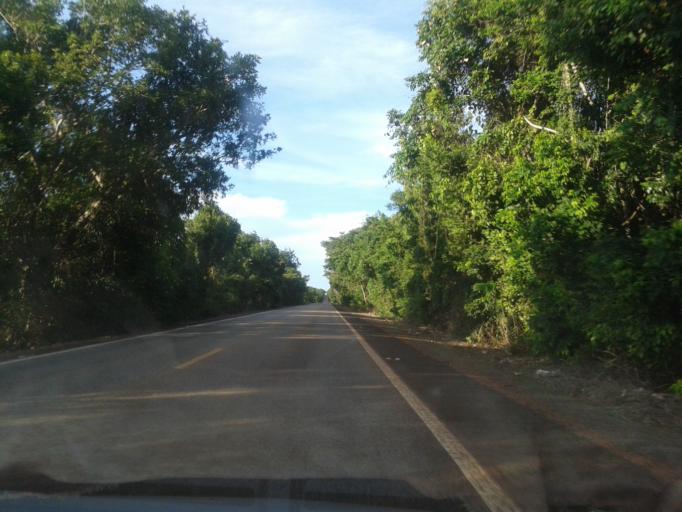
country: BR
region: Goias
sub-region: Sao Miguel Do Araguaia
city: Sao Miguel do Araguaia
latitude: -13.5206
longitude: -50.3032
